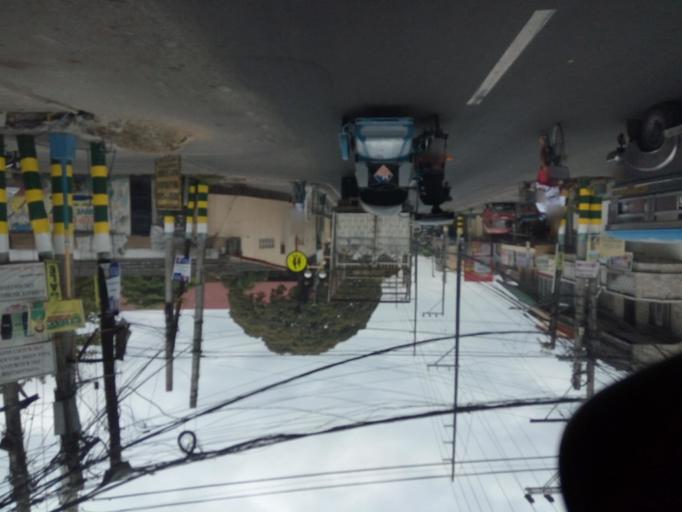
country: PH
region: Central Luzon
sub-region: Province of Bulacan
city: Pulilan
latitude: 14.9024
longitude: 120.8500
